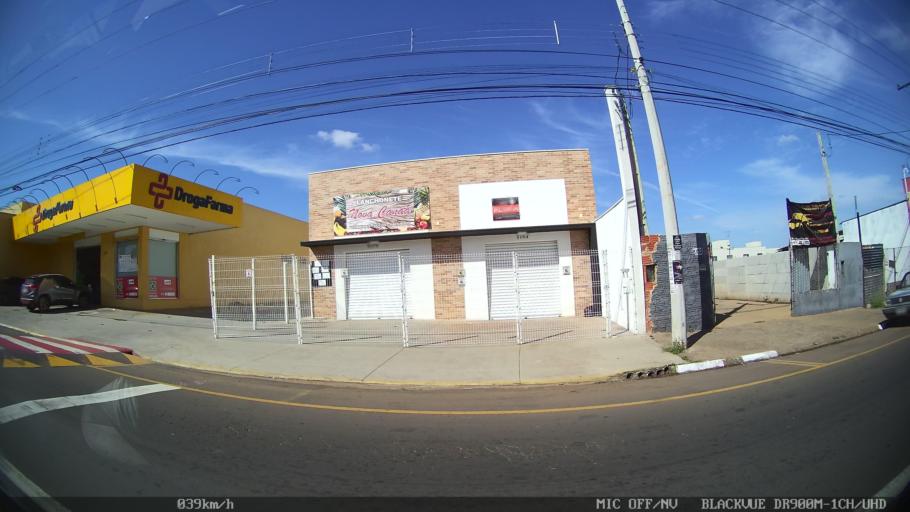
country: BR
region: Sao Paulo
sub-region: Franca
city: Franca
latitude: -20.5089
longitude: -47.3991
